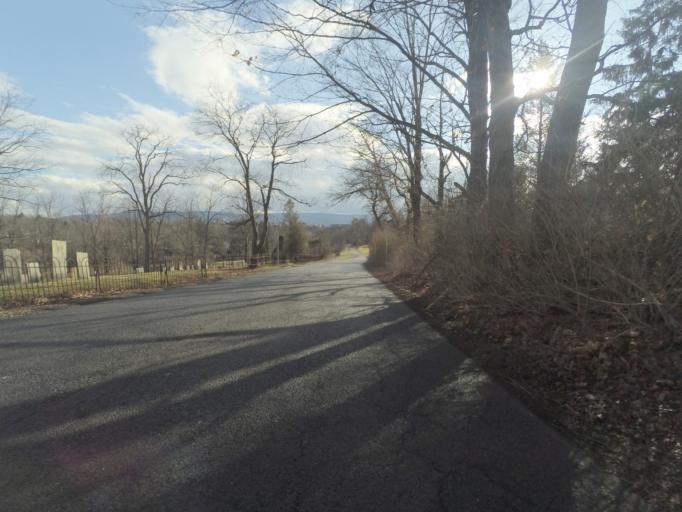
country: US
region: Pennsylvania
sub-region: Centre County
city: Lemont
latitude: 40.7966
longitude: -77.8346
